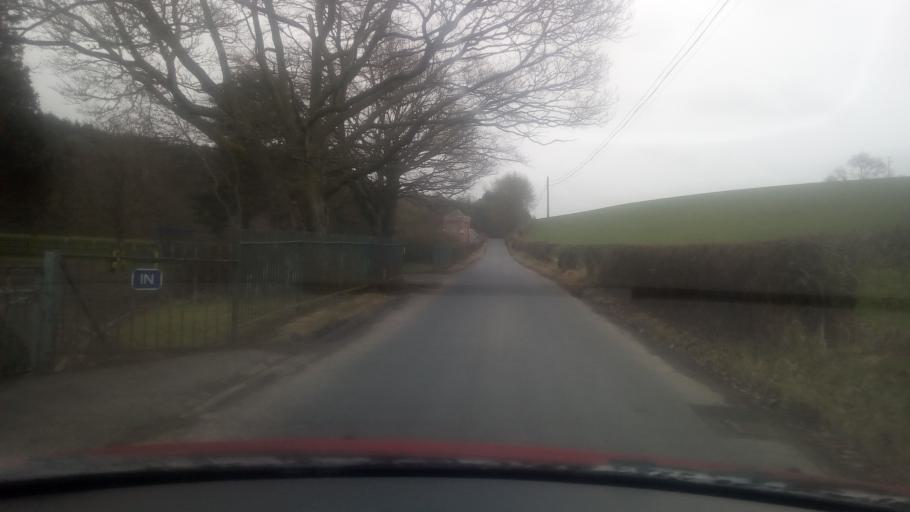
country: GB
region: Scotland
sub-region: The Scottish Borders
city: Jedburgh
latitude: 55.3928
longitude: -2.6545
